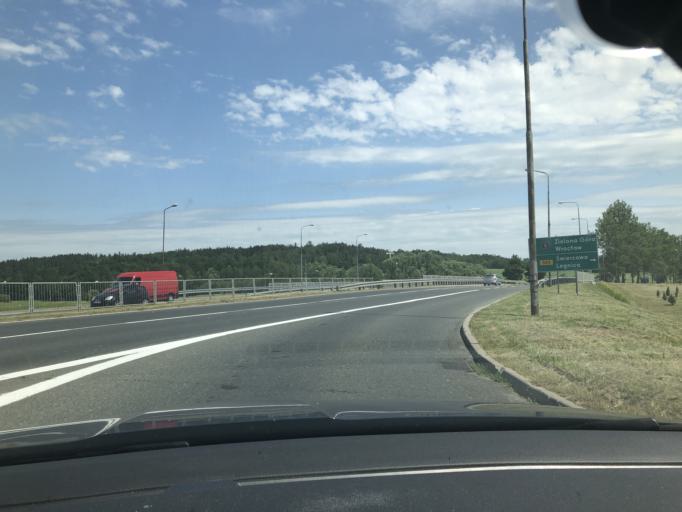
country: PL
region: Lower Silesian Voivodeship
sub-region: Powiat jeleniogorski
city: Jezow Sudecki
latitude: 50.9202
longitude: 15.7635
